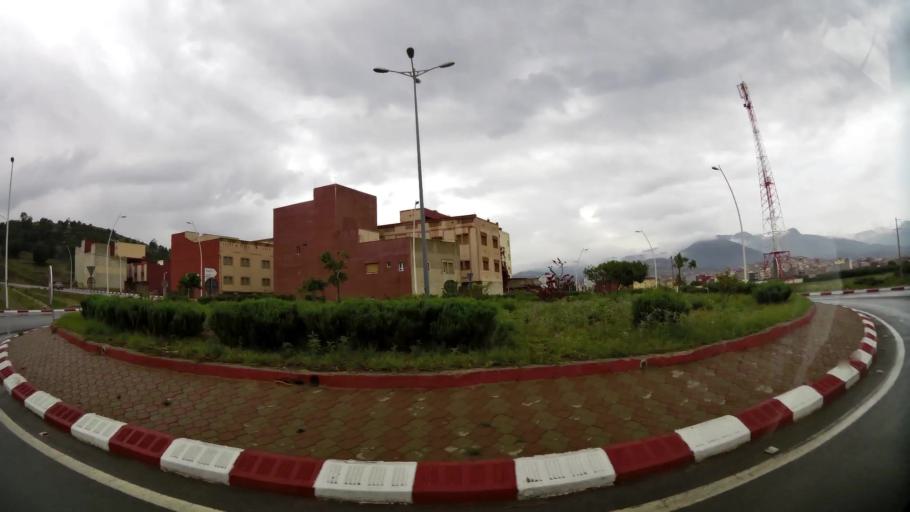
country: MA
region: Oriental
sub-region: Nador
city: Nador
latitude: 35.1456
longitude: -2.9766
